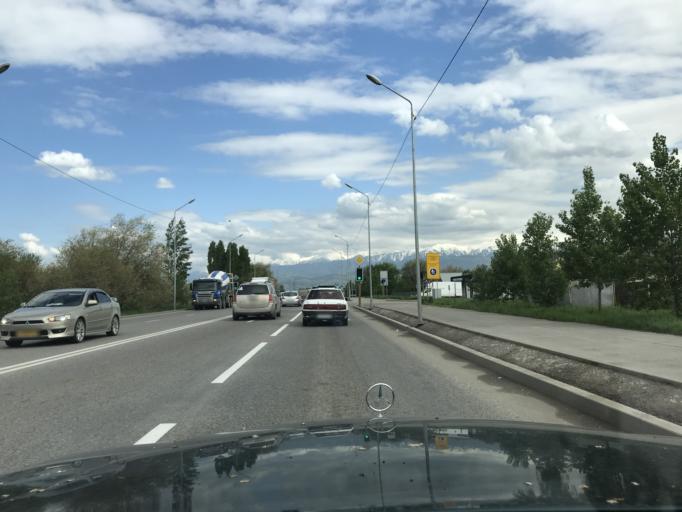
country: KZ
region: Almaty Oblysy
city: Burunday
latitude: 43.3083
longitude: 76.8747
